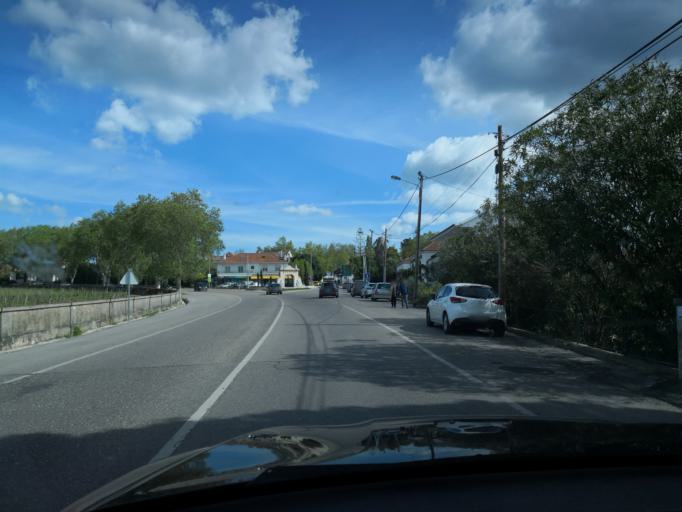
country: PT
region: Setubal
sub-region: Palmela
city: Quinta do Anjo
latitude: 38.5208
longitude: -9.0152
